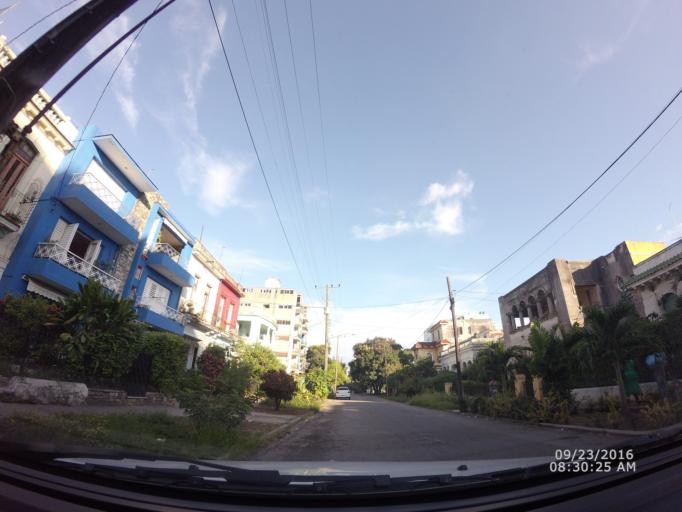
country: CU
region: La Habana
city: Havana
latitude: 23.1296
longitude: -82.3975
